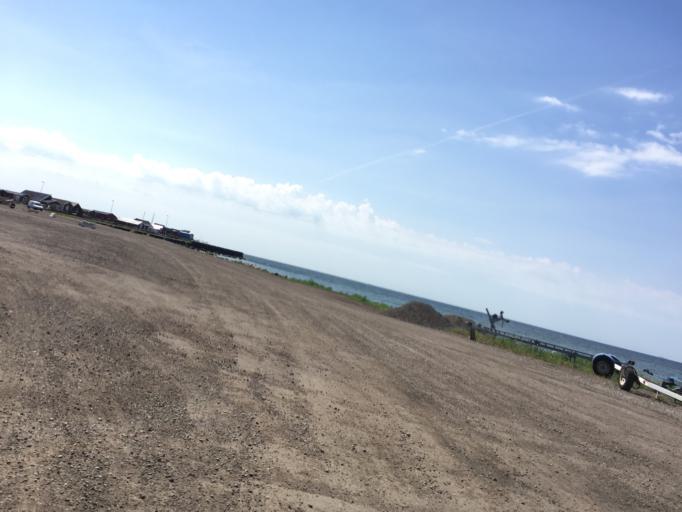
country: SE
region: Skane
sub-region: Trelleborgs Kommun
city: Trelleborg
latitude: 55.3569
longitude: 13.2271
